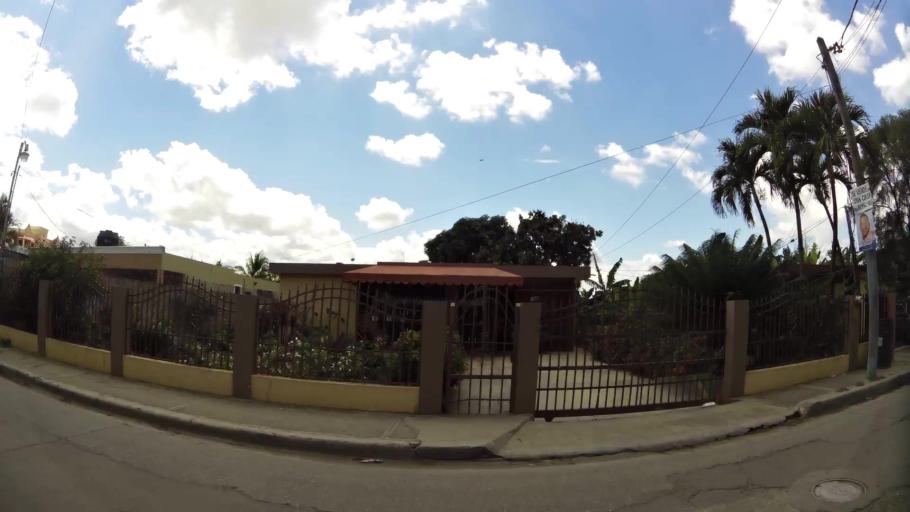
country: DO
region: Santiago
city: Santiago de los Caballeros
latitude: 19.4745
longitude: -70.6678
